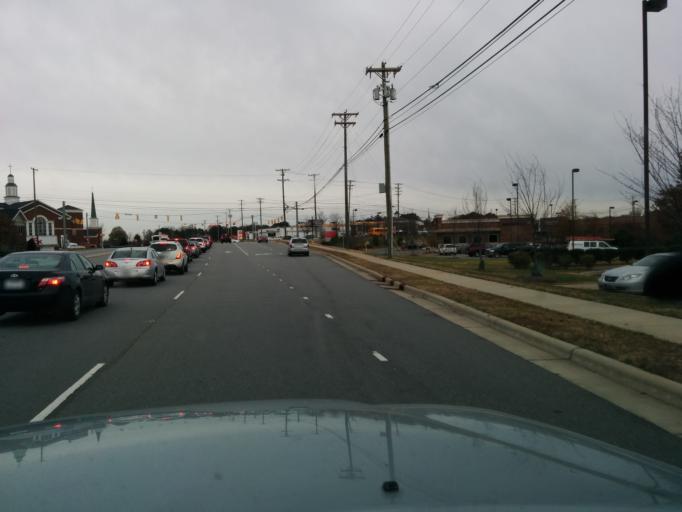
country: US
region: North Carolina
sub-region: Iredell County
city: Mooresville
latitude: 35.5855
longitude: -80.8742
